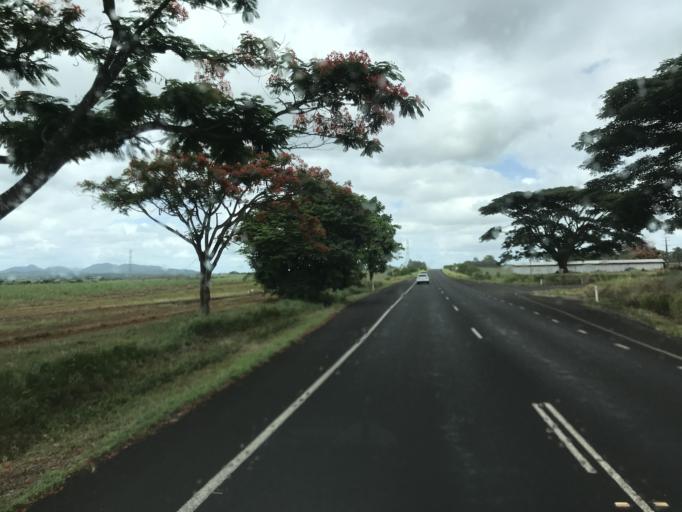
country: AU
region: Queensland
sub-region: Cassowary Coast
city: Innisfail
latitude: -17.5797
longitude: 145.9930
